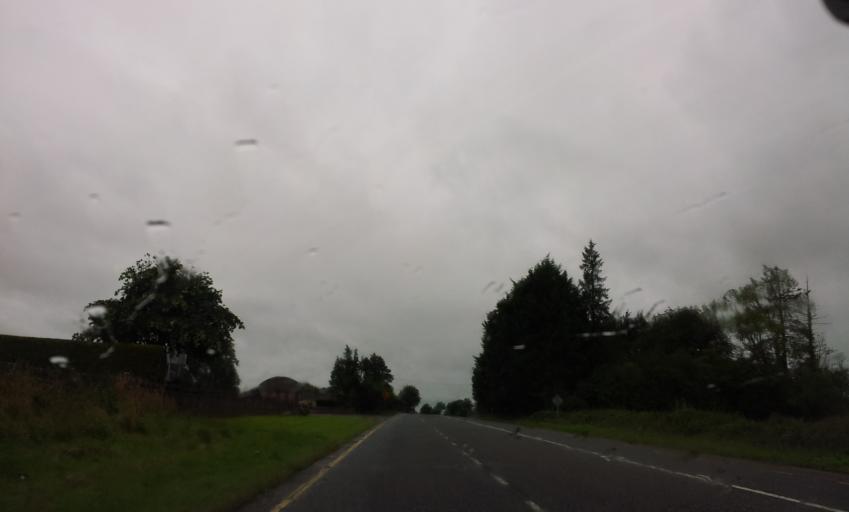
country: IE
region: Munster
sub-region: County Cork
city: Mitchelstown
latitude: 52.2771
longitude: -8.2578
